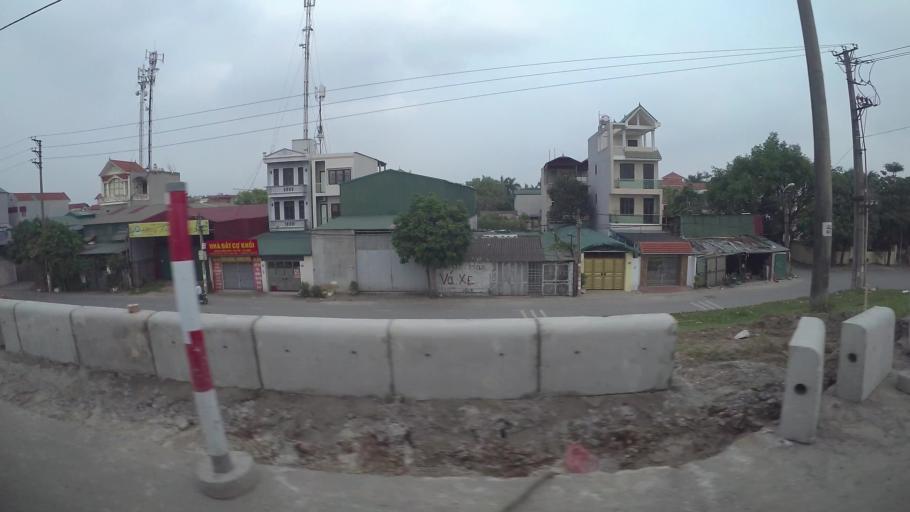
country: VN
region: Ha Noi
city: Trau Quy
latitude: 21.0125
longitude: 105.9044
